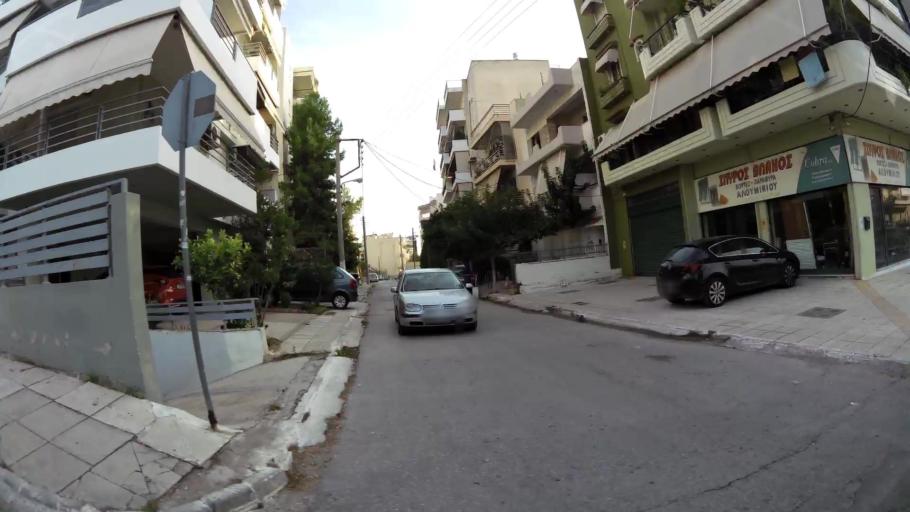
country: GR
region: Attica
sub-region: Nomarchia Athinas
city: Kamateron
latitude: 38.0584
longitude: 23.7087
